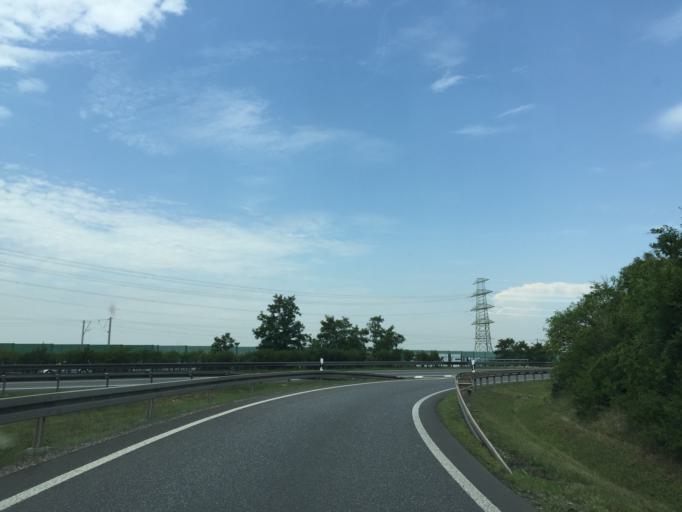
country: DE
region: Thuringia
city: Dornheim
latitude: 50.8246
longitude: 11.0059
